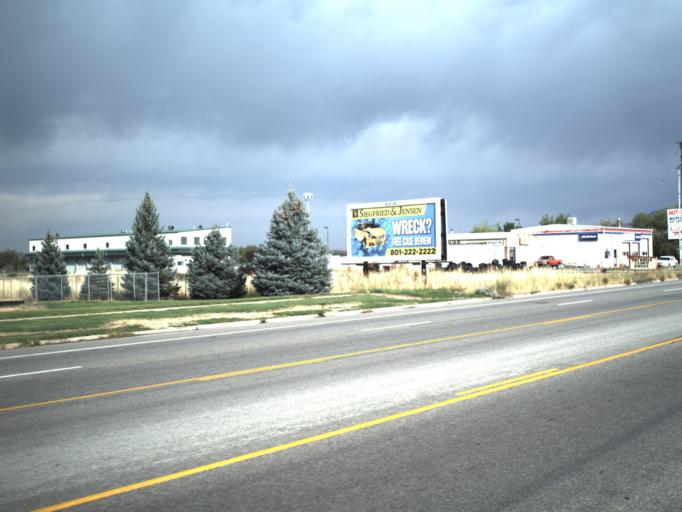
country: US
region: Utah
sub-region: Weber County
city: Harrisville
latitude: 41.2779
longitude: -111.9692
